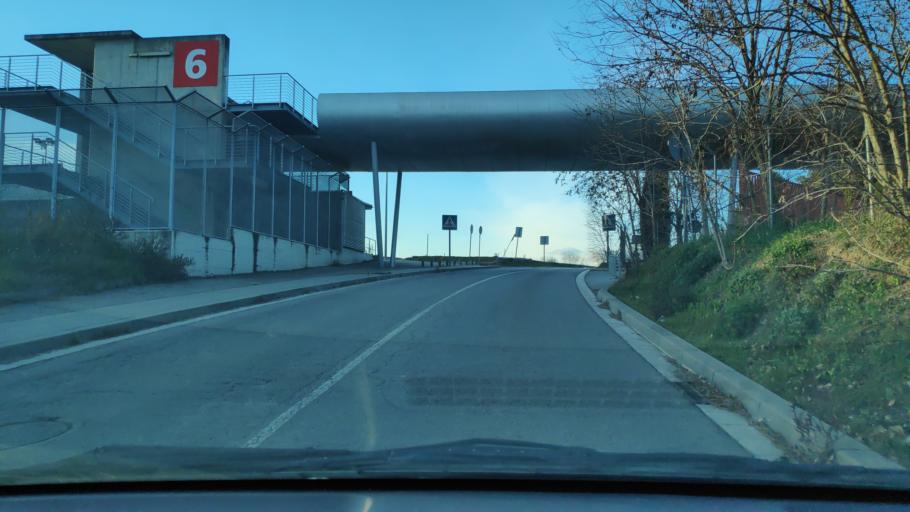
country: ES
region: Catalonia
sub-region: Provincia de Barcelona
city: Montmelo
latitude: 41.5635
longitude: 2.2522
